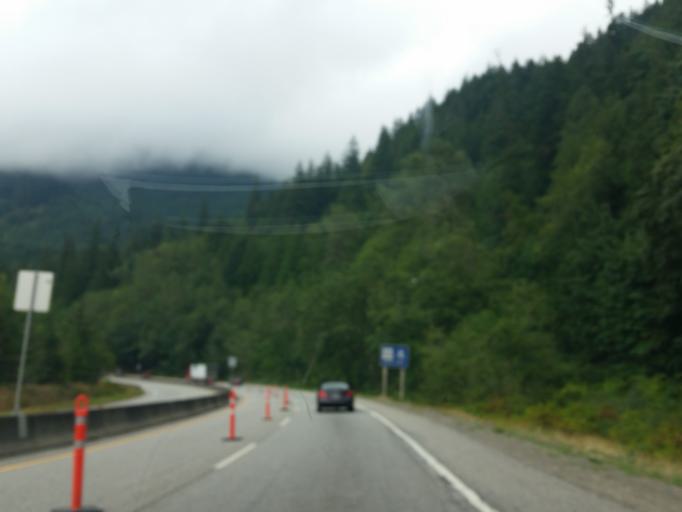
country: CA
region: British Columbia
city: Hope
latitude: 49.3788
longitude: -121.3230
